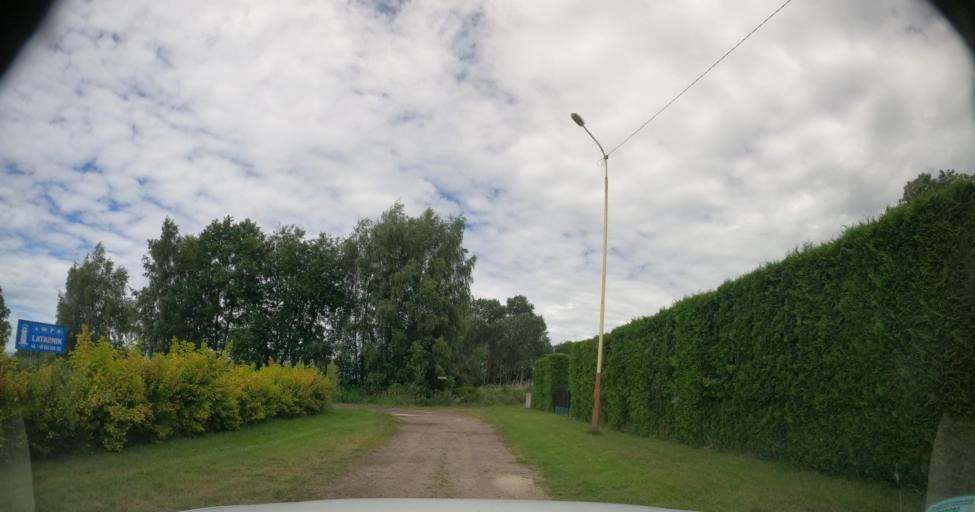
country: PL
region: West Pomeranian Voivodeship
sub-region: Powiat goleniowski
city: Stepnica
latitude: 53.6984
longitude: 14.5447
